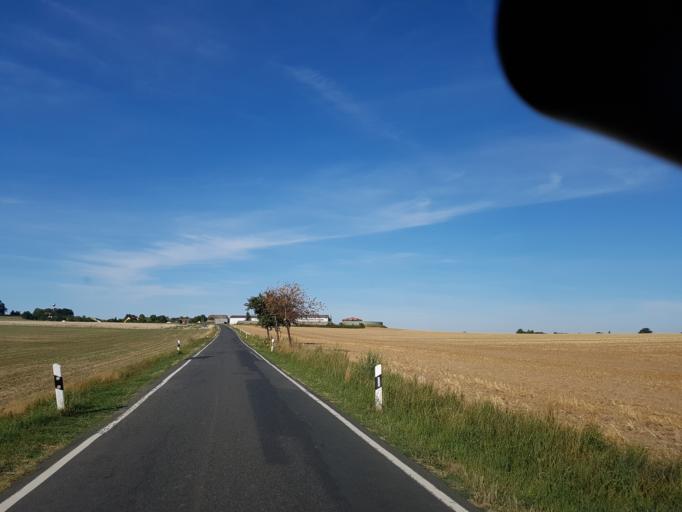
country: DE
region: Saxony
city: Naundorf
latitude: 51.2379
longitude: 13.1391
